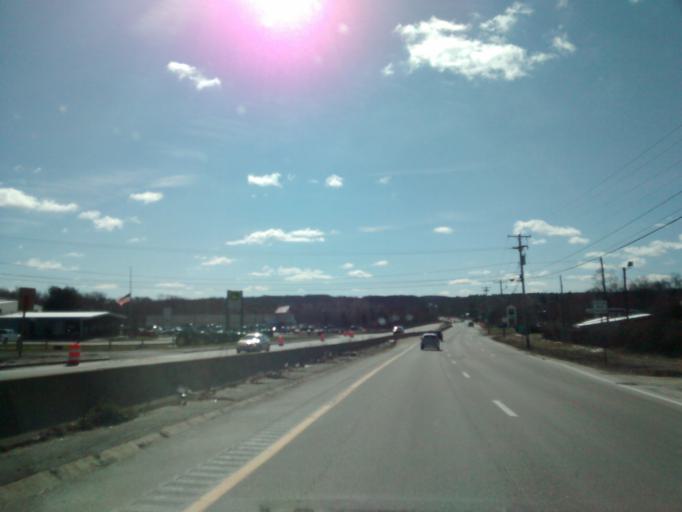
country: US
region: Massachusetts
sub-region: Worcester County
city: Millbury
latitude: 42.1936
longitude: -71.7715
